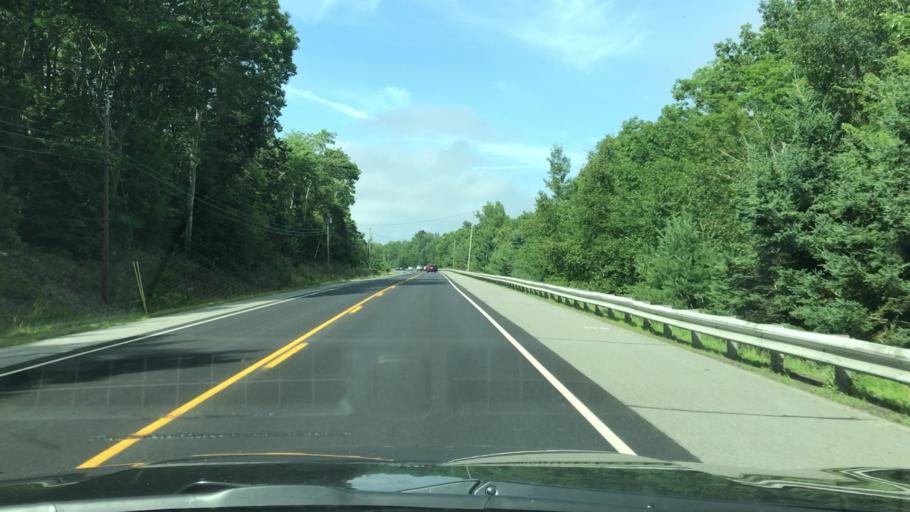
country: US
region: Maine
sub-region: Hancock County
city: Bucksport
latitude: 44.5293
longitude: -68.8090
